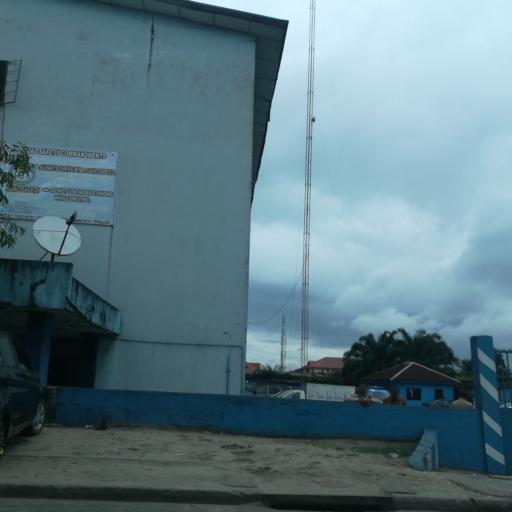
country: NG
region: Rivers
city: Port Harcourt
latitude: 4.7954
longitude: 7.0034
